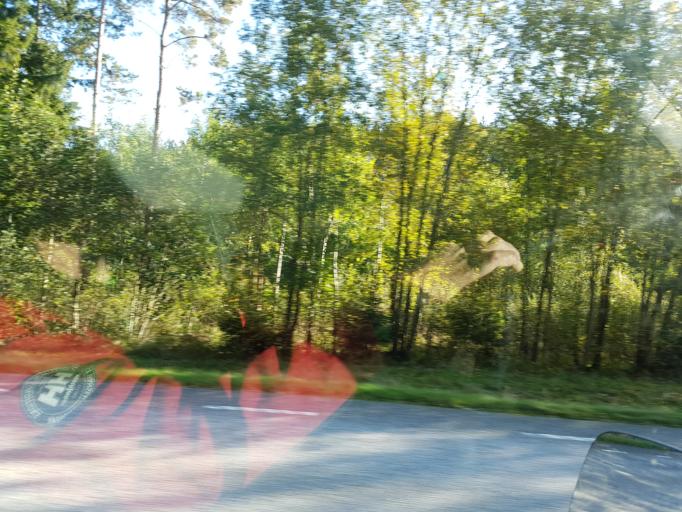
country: SE
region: Vaestra Goetaland
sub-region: Orust
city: Henan
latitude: 58.1500
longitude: 11.7060
